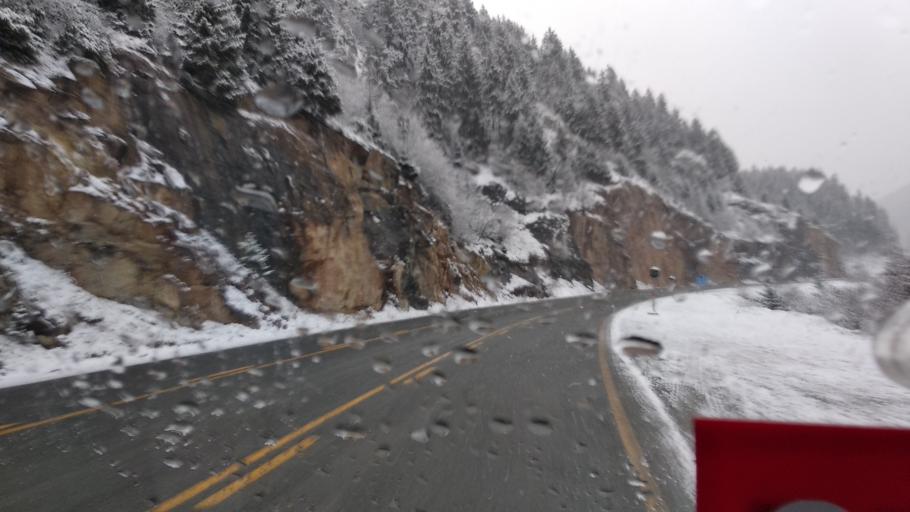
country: TR
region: Gumushane
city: Yaglidere
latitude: 40.6780
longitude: 39.4395
